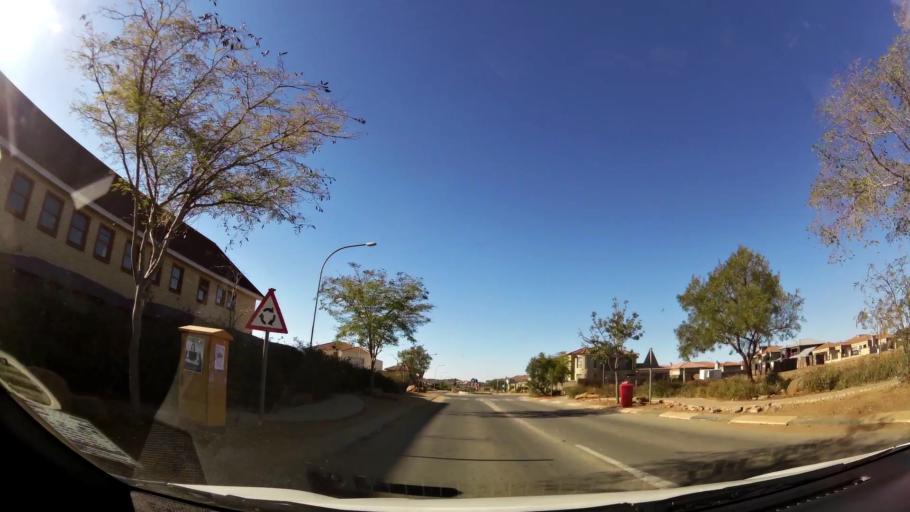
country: ZA
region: Limpopo
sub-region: Capricorn District Municipality
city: Polokwane
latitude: -23.9103
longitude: 29.5038
